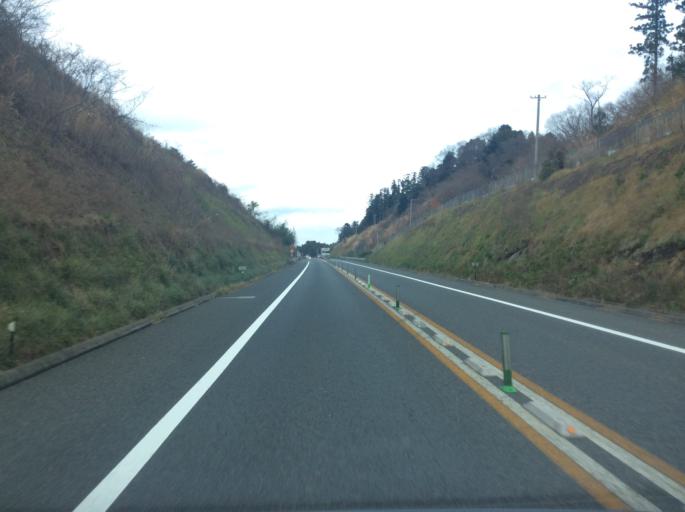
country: JP
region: Fukushima
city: Iwaki
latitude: 37.1495
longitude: 140.9654
